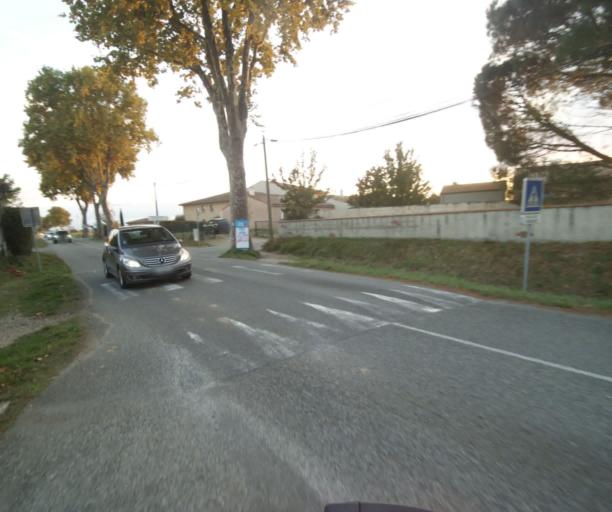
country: FR
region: Midi-Pyrenees
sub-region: Departement du Tarn-et-Garonne
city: Verdun-sur-Garonne
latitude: 43.8429
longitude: 1.2391
